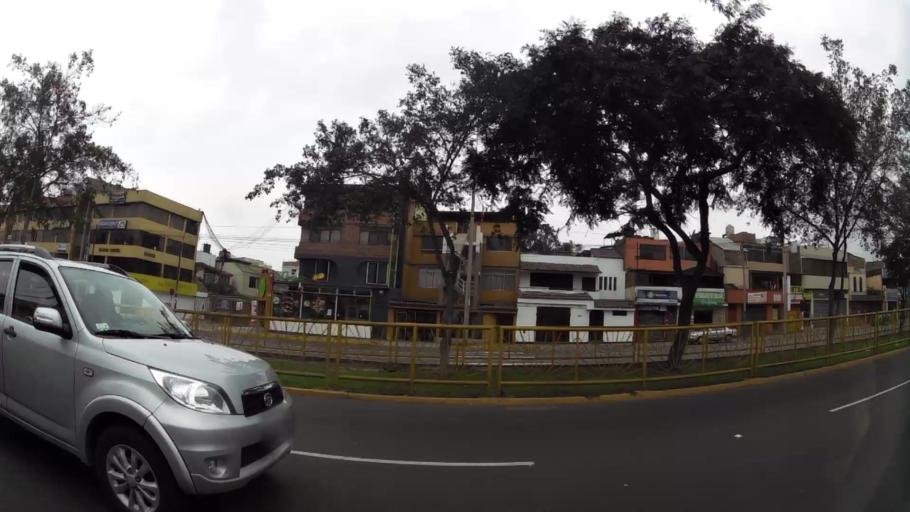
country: PE
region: Lima
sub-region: Lima
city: San Luis
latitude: -12.0803
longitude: -76.9928
